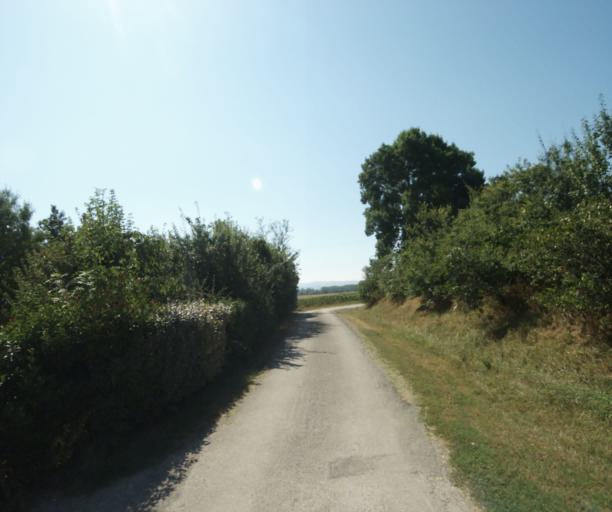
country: FR
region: Midi-Pyrenees
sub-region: Departement de la Haute-Garonne
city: Revel
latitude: 43.5079
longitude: 1.9559
